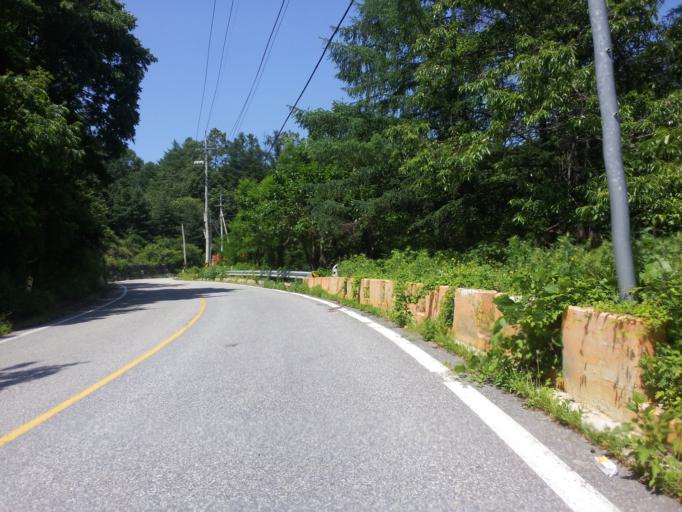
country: KR
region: Chungcheongbuk-do
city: Okcheon
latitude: 36.4427
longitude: 127.6464
